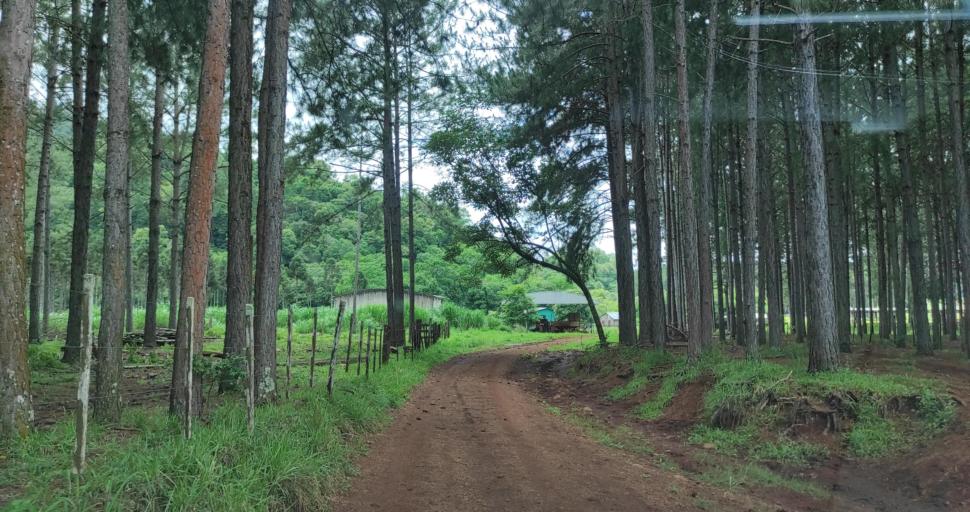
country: AR
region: Misiones
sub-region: Departamento de Veinticinco de Mayo
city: Veinticinco de Mayo
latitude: -27.4195
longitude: -54.7035
